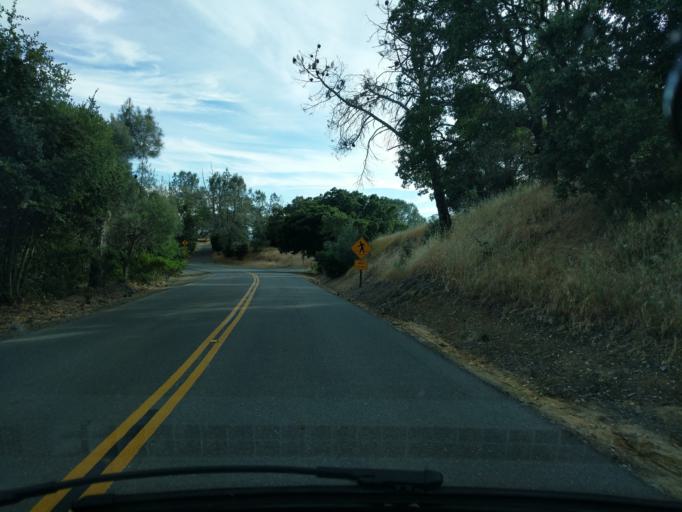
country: US
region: California
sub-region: Contra Costa County
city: Diablo
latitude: 37.8514
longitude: -121.9293
